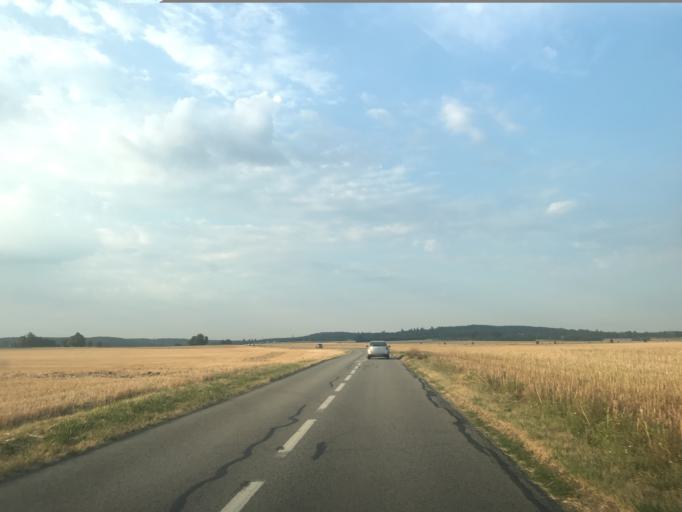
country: FR
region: Ile-de-France
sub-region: Departement des Yvelines
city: Villiers-Saint-Frederic
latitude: 48.8033
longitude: 1.8677
